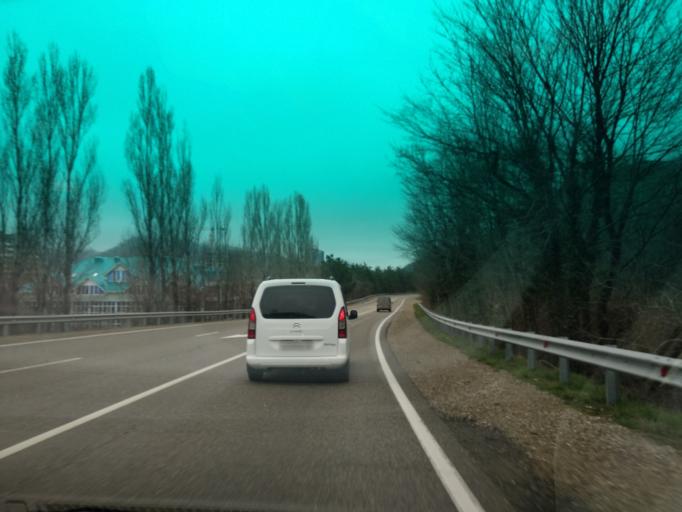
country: RU
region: Krasnodarskiy
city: Ol'ginka
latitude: 44.1911
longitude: 38.8890
